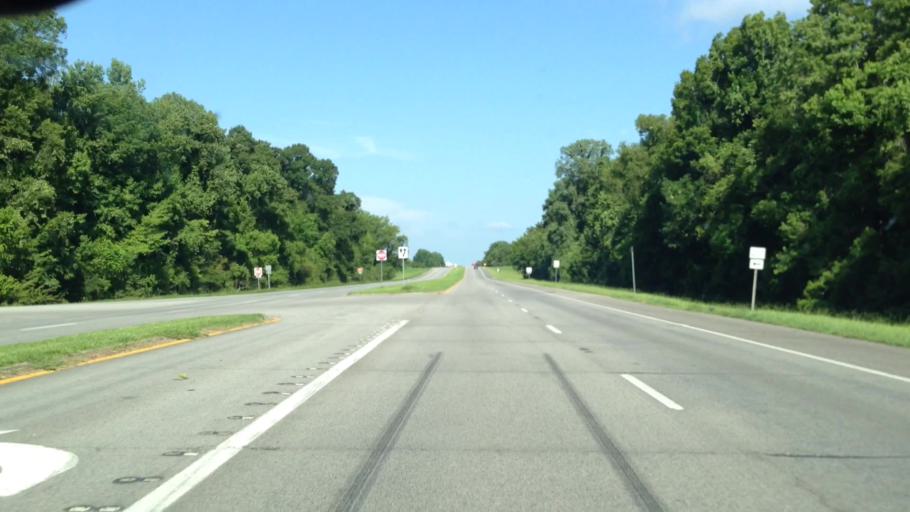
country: US
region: Louisiana
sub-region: Saint Landry Parish
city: Krotz Springs
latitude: 30.5396
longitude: -91.7721
